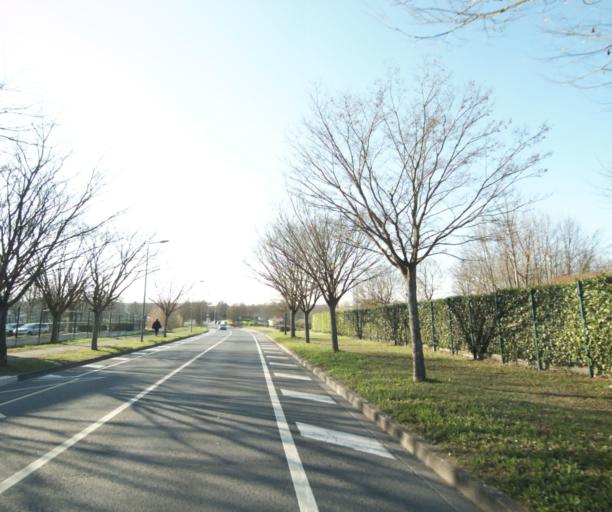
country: FR
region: Ile-de-France
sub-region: Departement du Val-d'Oise
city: Osny
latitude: 49.0550
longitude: 2.0402
